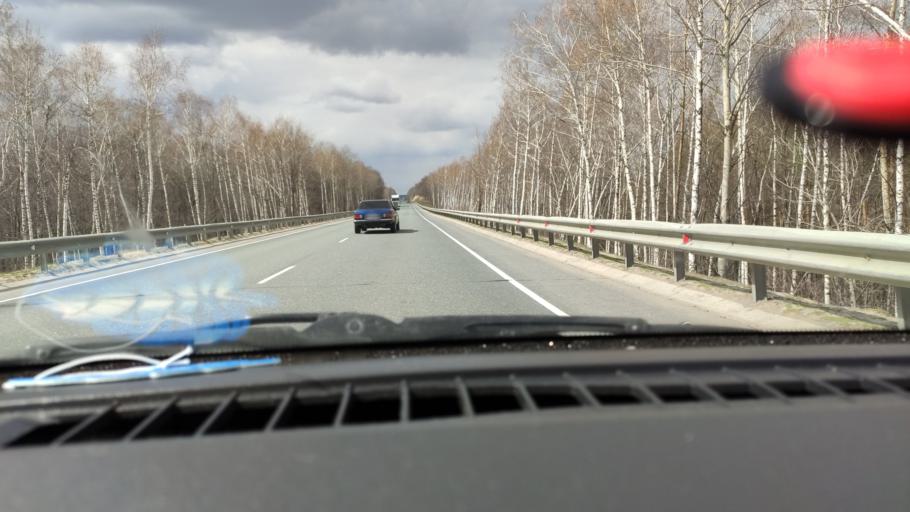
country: RU
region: Saratov
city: Vol'sk
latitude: 52.1110
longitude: 47.3399
